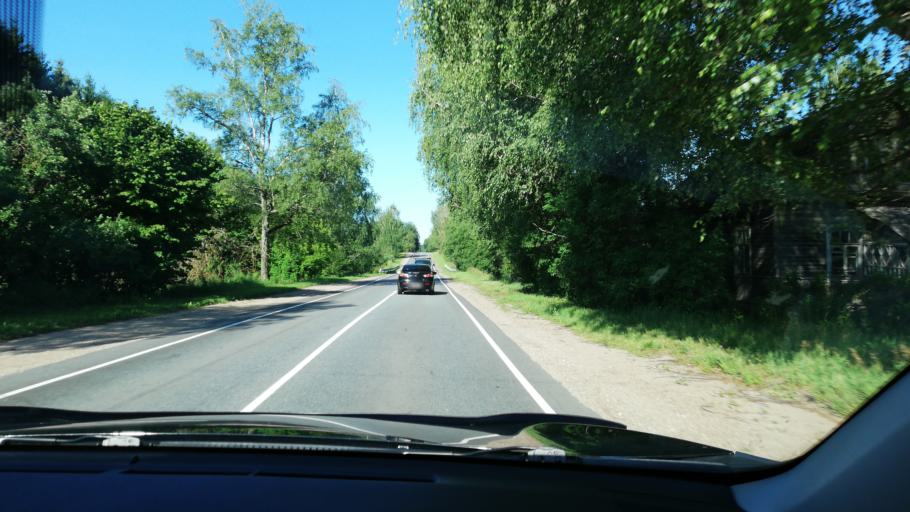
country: RU
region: Pskov
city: Nevel'
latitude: 56.0324
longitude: 30.1210
